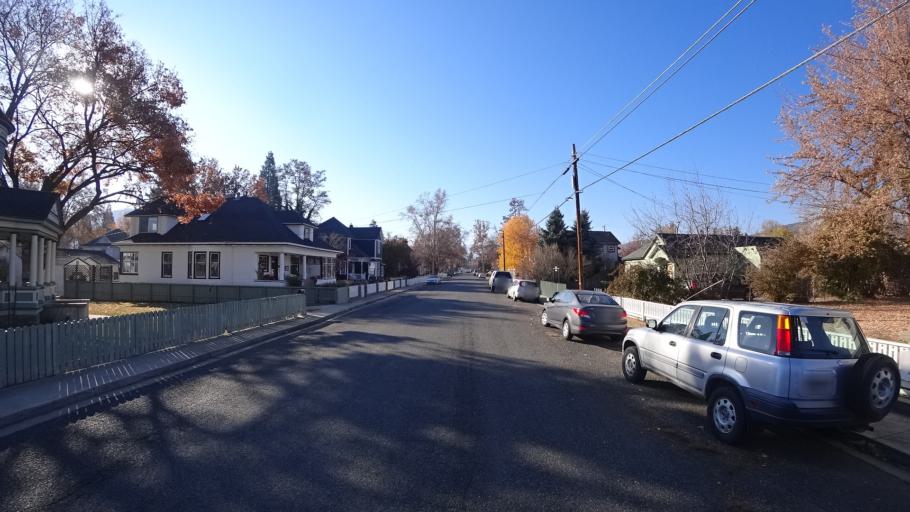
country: US
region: California
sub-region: Siskiyou County
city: Yreka
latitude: 41.7359
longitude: -122.6355
